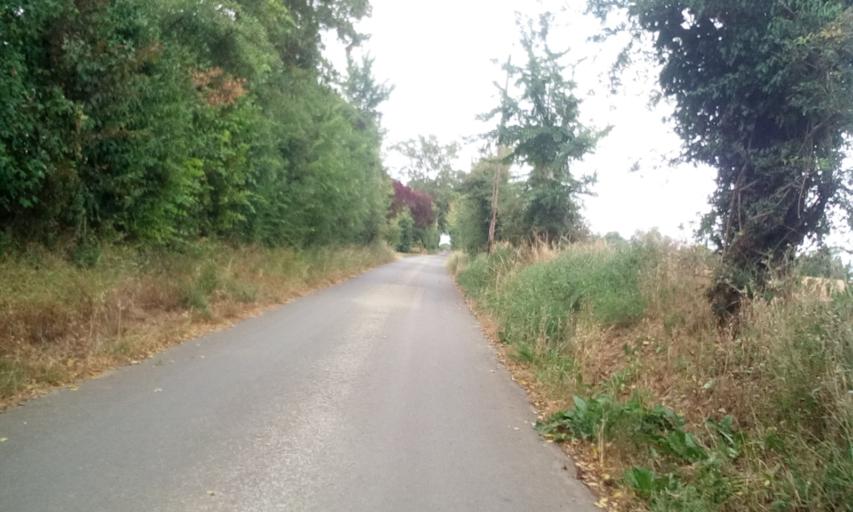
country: FR
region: Lower Normandy
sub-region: Departement du Calvados
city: Thury-Harcourt
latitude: 48.9807
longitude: -0.4237
